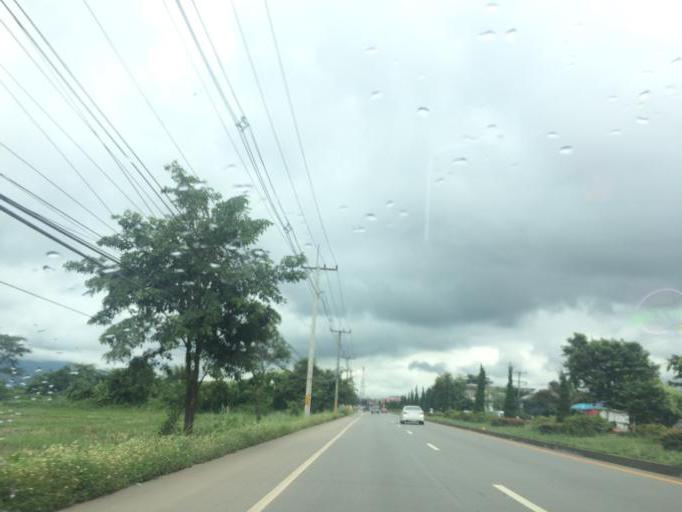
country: TH
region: Chiang Rai
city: Mae Chan
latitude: 20.0368
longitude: 99.8751
